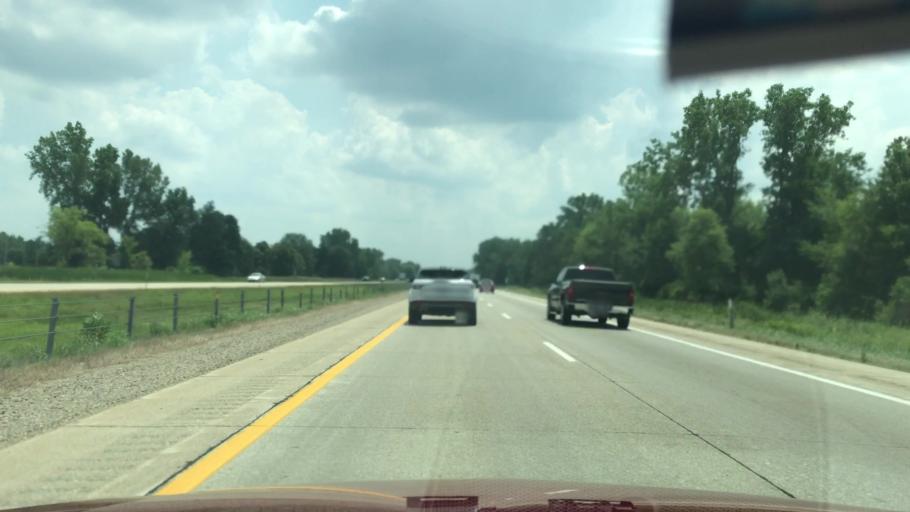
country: US
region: Michigan
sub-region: Allegan County
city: Plainwell
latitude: 42.4250
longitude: -85.6608
